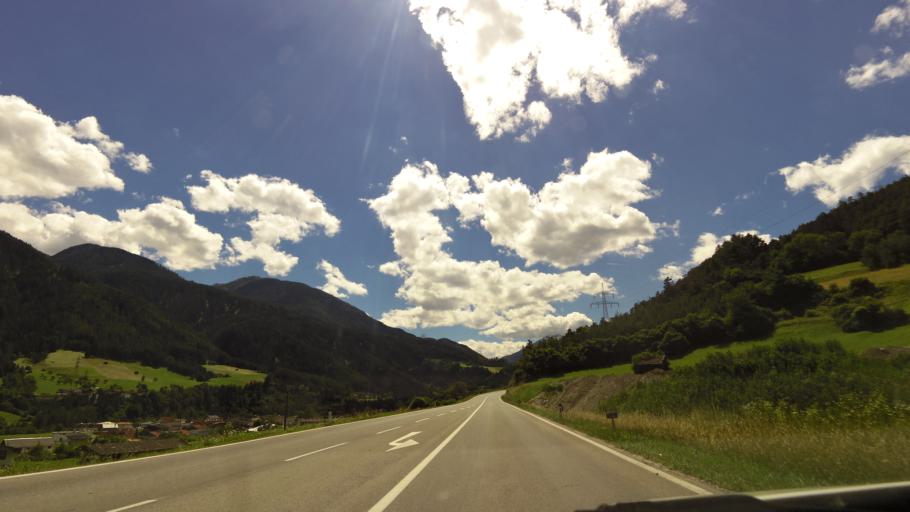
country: AT
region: Tyrol
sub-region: Politischer Bezirk Imst
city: Roppen
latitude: 47.2206
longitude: 10.8133
